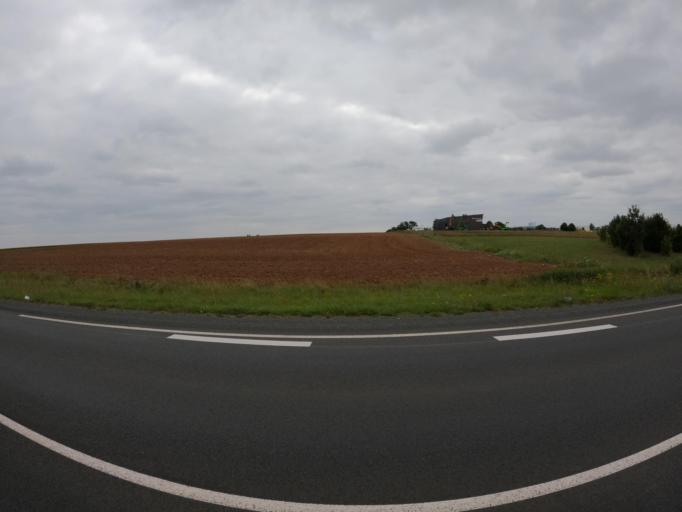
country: FR
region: Pays de la Loire
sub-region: Departement de la Vendee
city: Fontenay-le-Comte
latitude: 46.4452
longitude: -0.8077
